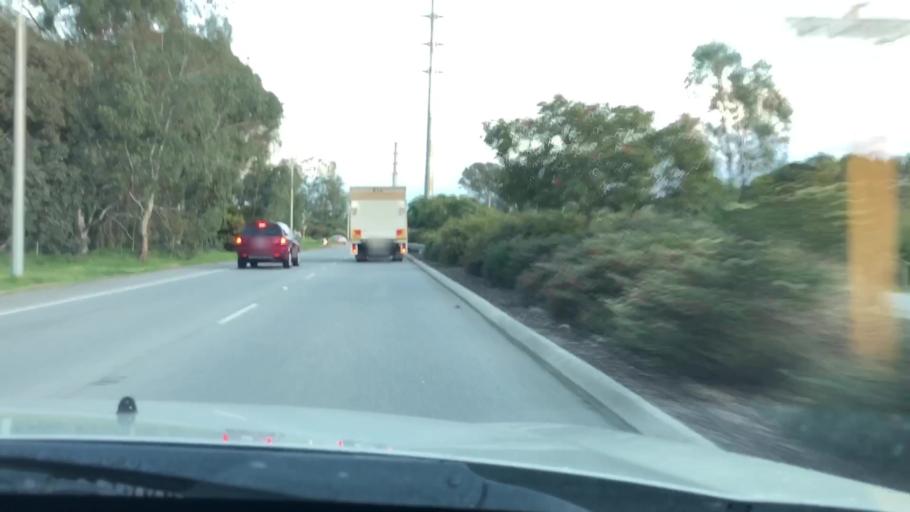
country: AU
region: Western Australia
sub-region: Armadale
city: Harrisdale
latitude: -32.1162
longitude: 115.9485
